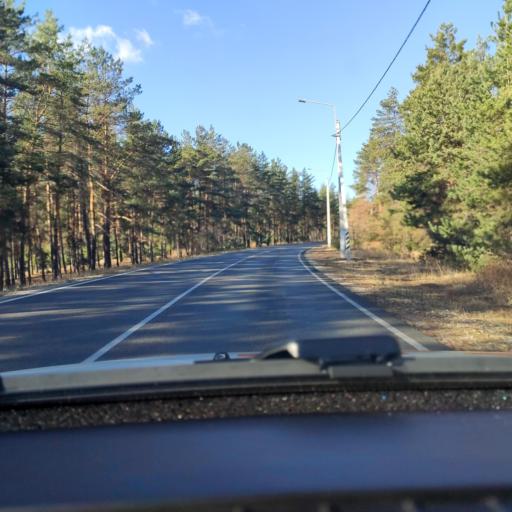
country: RU
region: Voronezj
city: Shilovo
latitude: 51.5277
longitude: 39.1444
